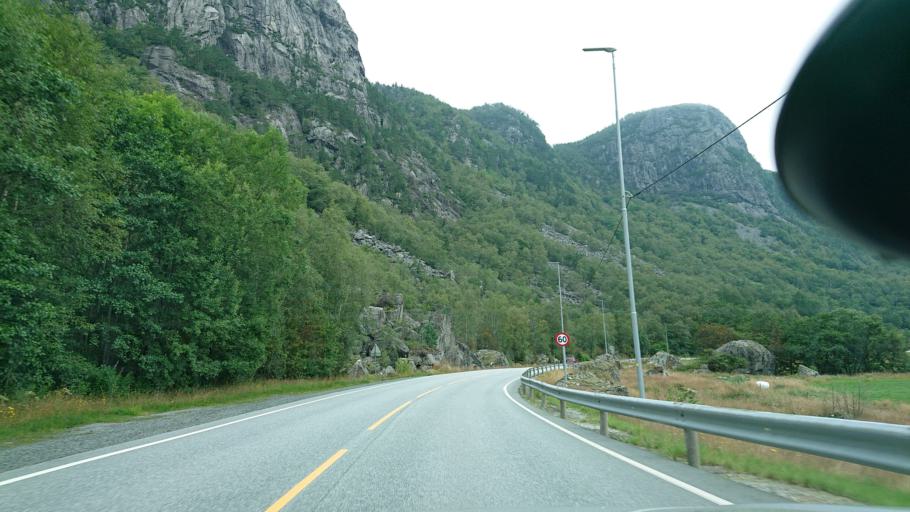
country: NO
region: Rogaland
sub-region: Hjelmeland
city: Hjelmelandsvagen
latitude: 59.1046
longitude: 6.1666
